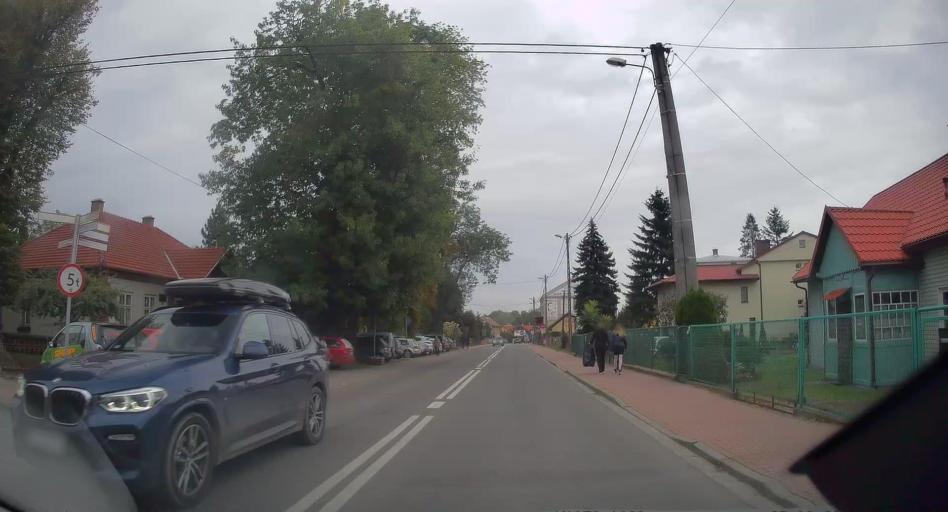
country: PL
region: Lesser Poland Voivodeship
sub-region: Powiat wielicki
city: Niepolomice
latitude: 50.0320
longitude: 20.2115
